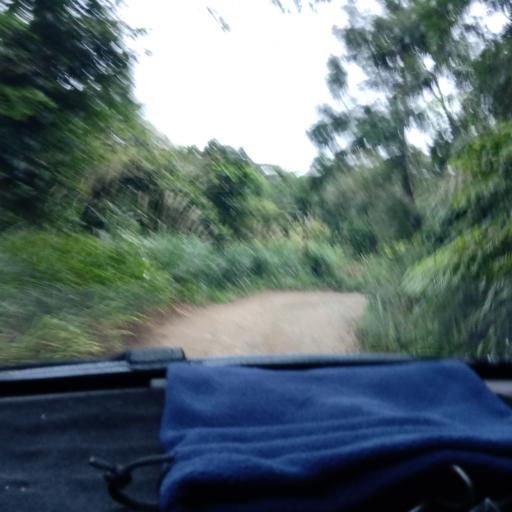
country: TW
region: Taiwan
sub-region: Yilan
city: Yilan
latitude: 24.8099
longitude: 121.6937
